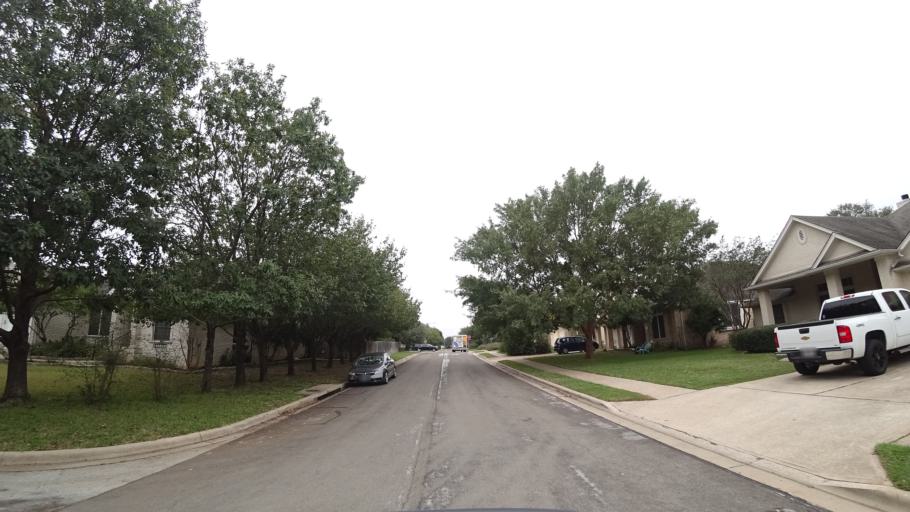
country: US
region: Texas
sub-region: Travis County
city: Shady Hollow
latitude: 30.2097
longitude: -97.8836
